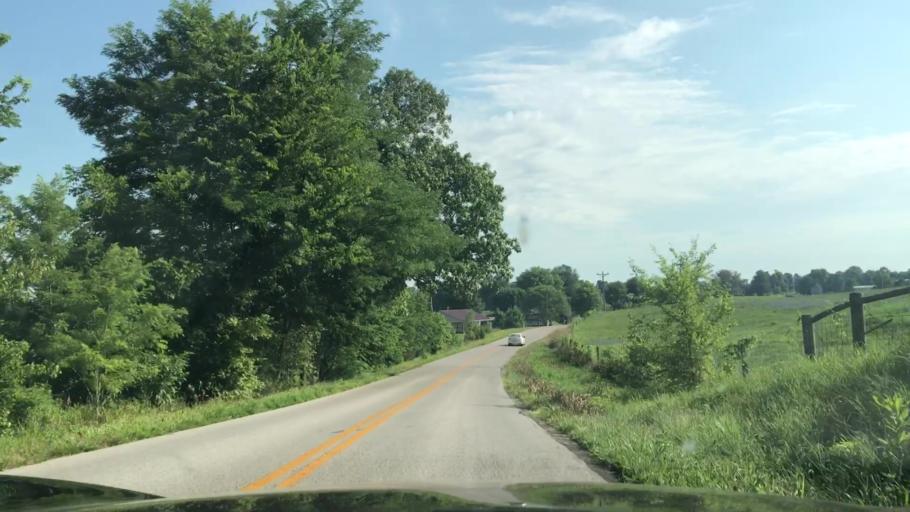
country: US
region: Kentucky
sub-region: Hart County
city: Munfordville
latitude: 37.2037
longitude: -85.7454
